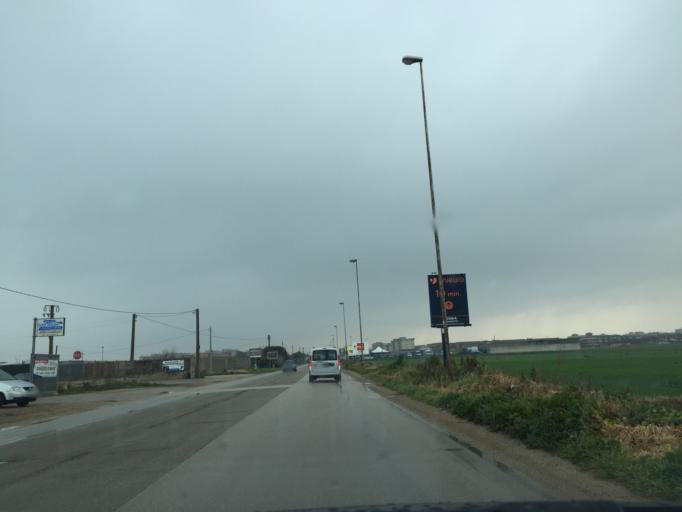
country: IT
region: Apulia
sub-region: Provincia di Foggia
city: Foggia
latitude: 41.4704
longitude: 15.5134
